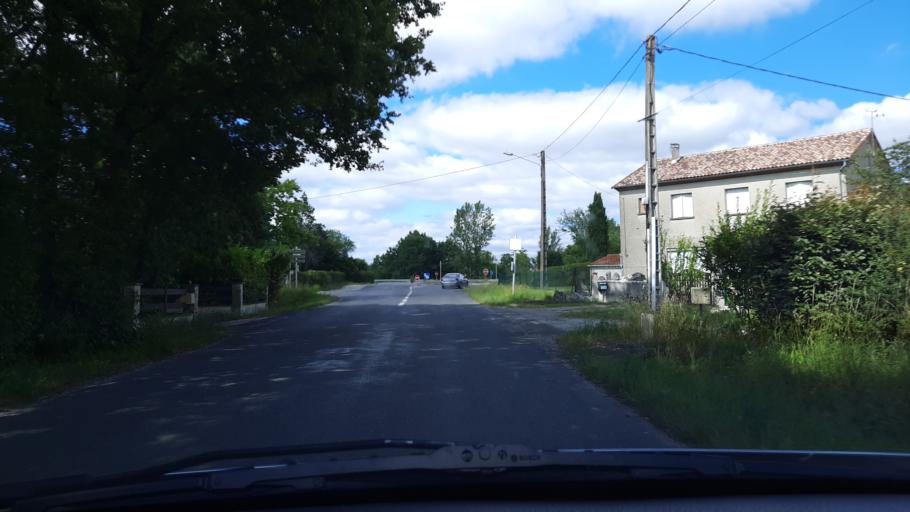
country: FR
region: Midi-Pyrenees
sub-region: Departement du Lot
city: Lalbenque
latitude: 44.2991
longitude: 1.4685
